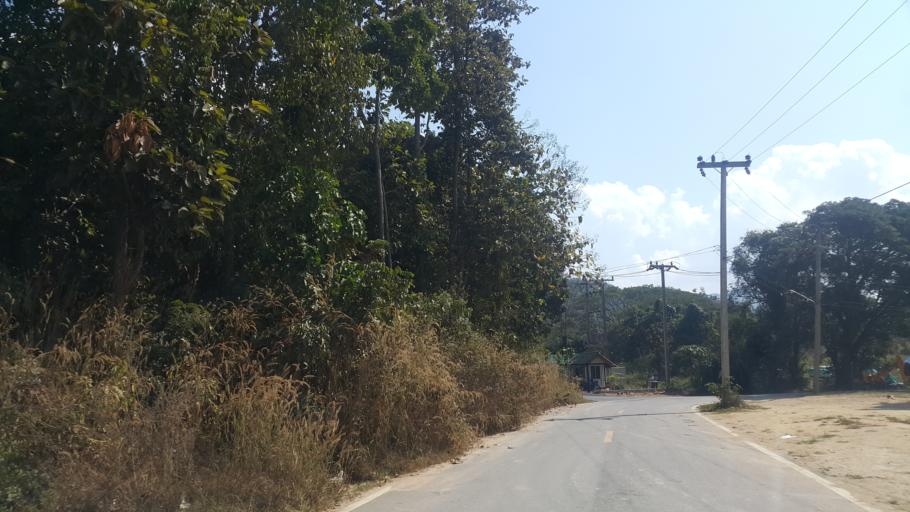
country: TH
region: Lamphun
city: Ban Thi
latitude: 18.6847
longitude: 99.1690
